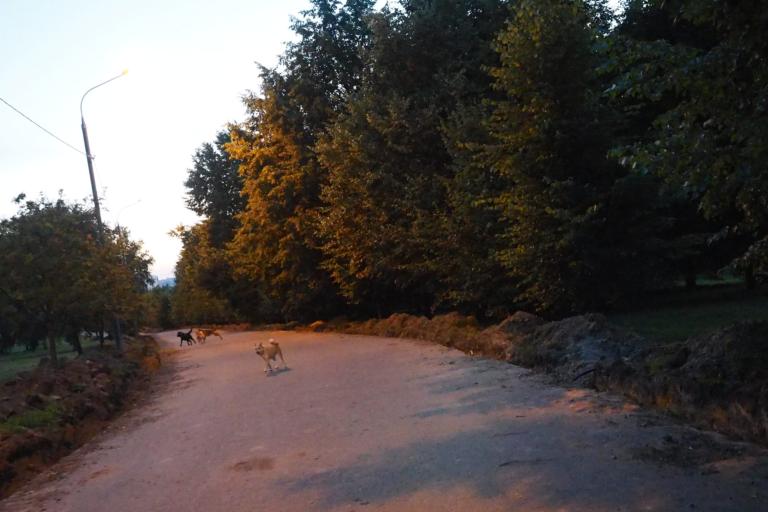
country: RU
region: Moscow
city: Ramenki
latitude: 55.6869
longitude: 37.5038
